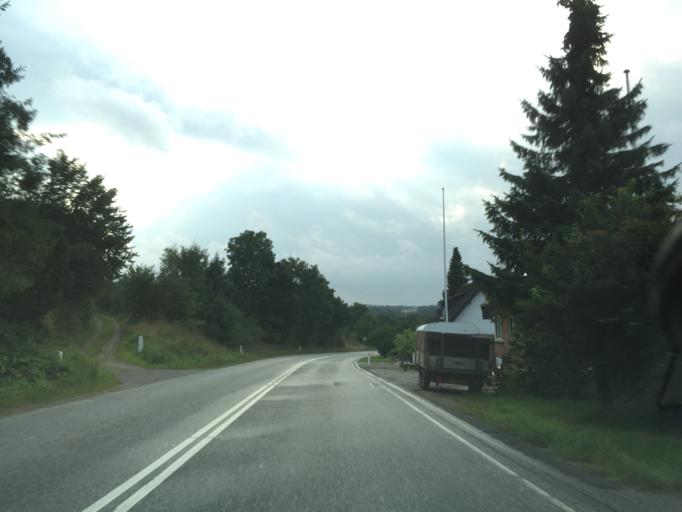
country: DK
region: Central Jutland
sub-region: Skanderborg Kommune
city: Galten
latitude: 56.1197
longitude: 9.8636
